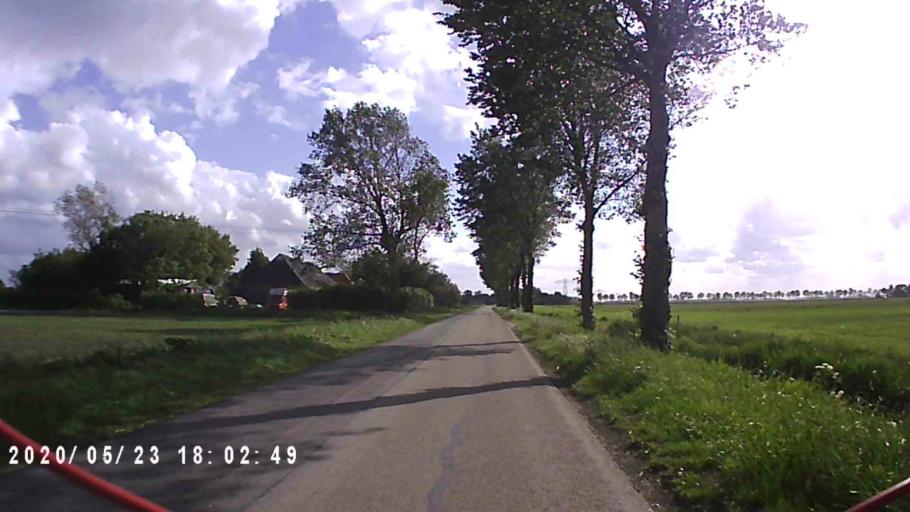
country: NL
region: Groningen
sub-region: Gemeente Slochteren
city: Slochteren
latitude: 53.2461
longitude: 6.7269
